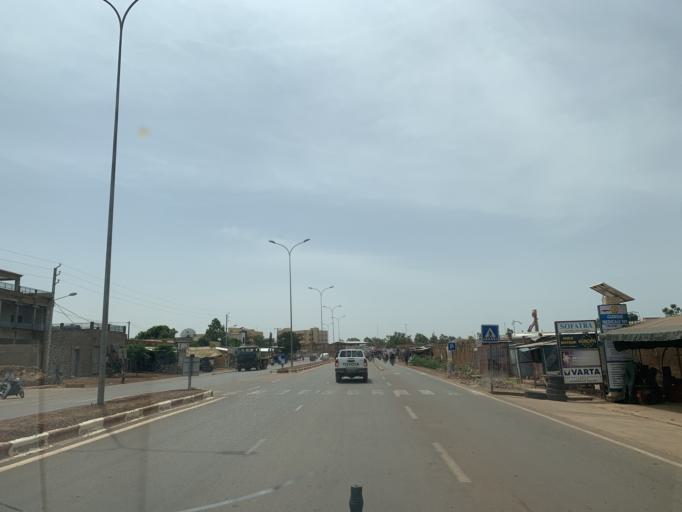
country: BF
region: Centre
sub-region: Kadiogo Province
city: Ouagadougou
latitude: 12.3370
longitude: -1.5060
